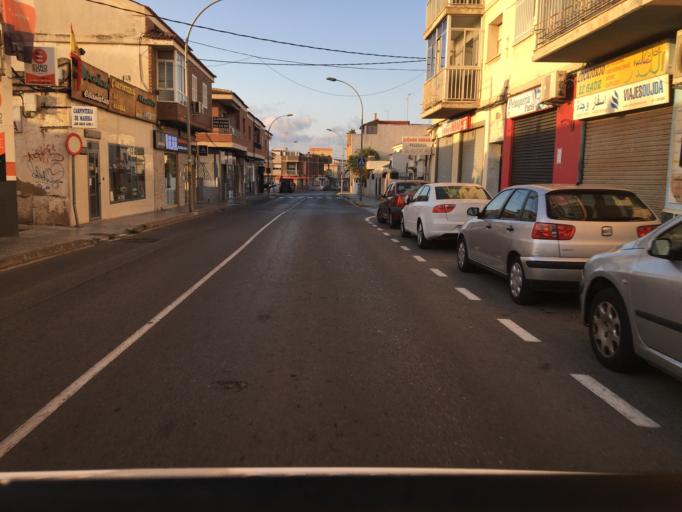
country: ES
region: Murcia
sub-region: Murcia
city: Cartagena
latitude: 37.6211
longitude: -0.9887
